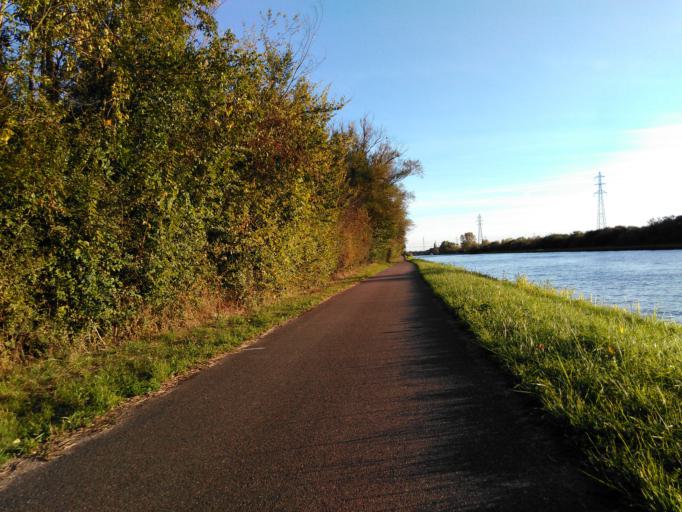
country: FR
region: Lorraine
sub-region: Departement de la Moselle
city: Talange
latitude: 49.2157
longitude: 6.1823
